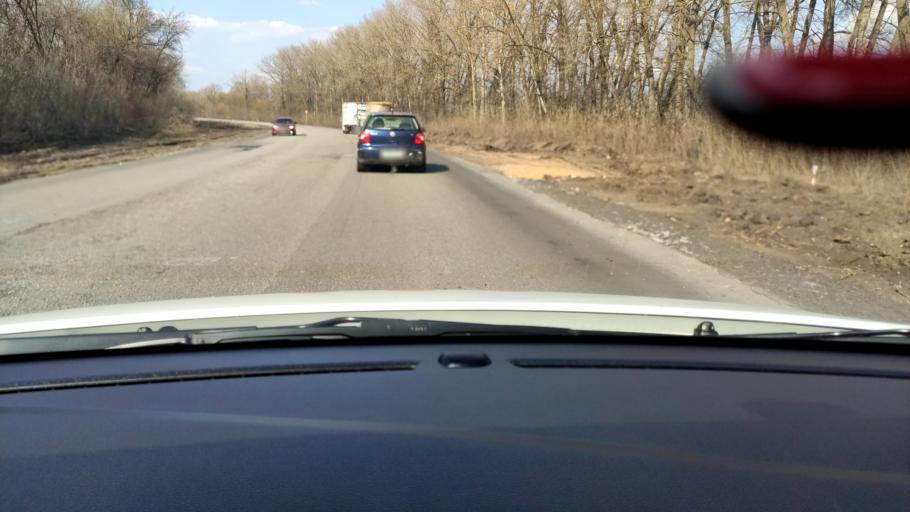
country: RU
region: Voronezj
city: Uryv-Pokrovka
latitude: 51.1884
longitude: 39.0868
